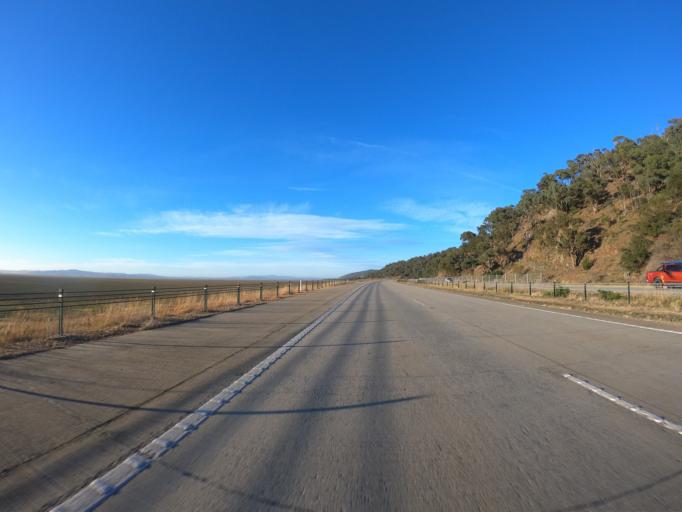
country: AU
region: New South Wales
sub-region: Yass Valley
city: Gundaroo
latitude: -35.0834
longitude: 149.3748
